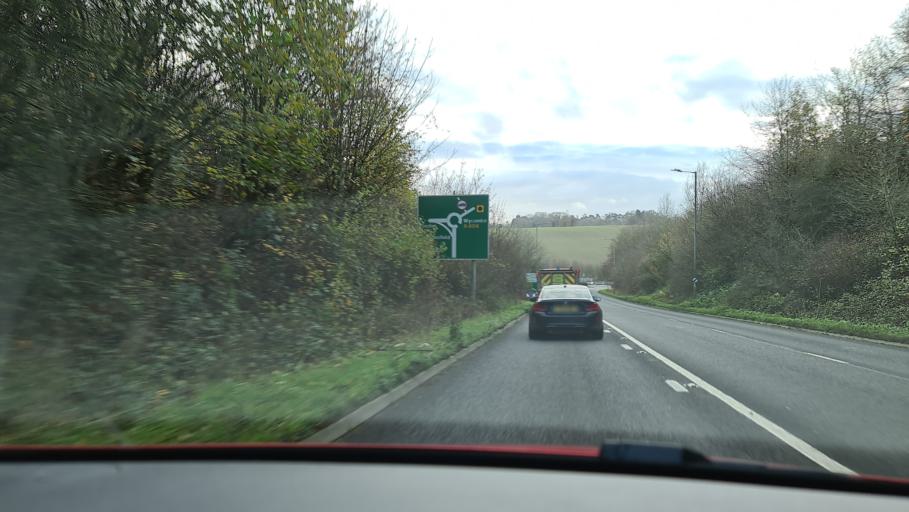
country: GB
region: England
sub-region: Buckinghamshire
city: Amersham
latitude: 51.6630
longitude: -0.6242
